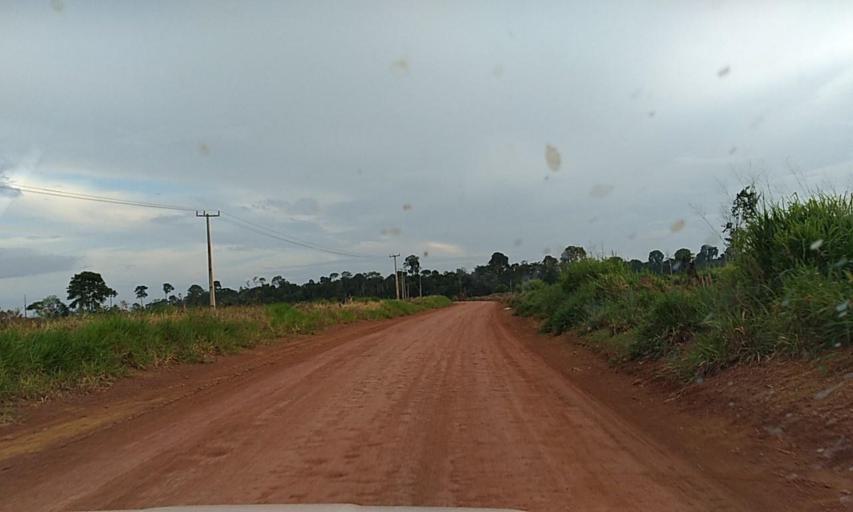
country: BR
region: Para
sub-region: Senador Jose Porfirio
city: Senador Jose Porfirio
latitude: -2.6965
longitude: -51.8223
